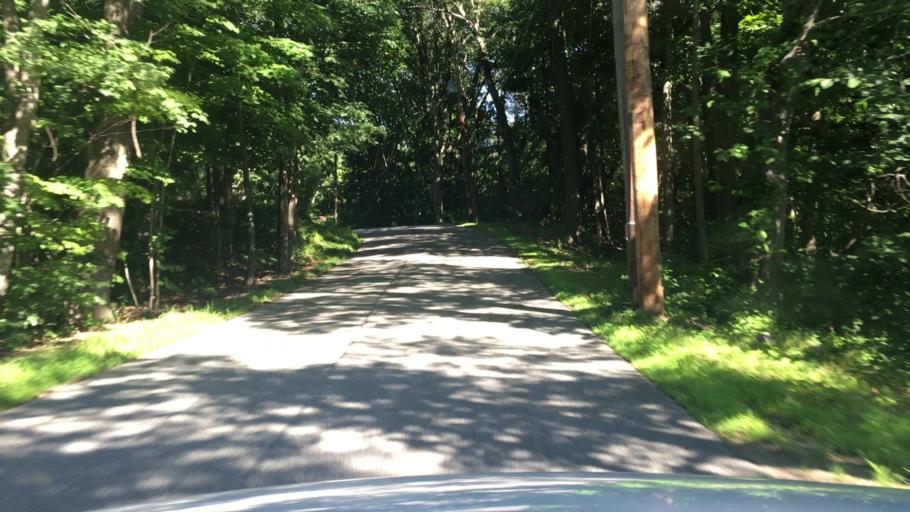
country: US
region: New Hampshire
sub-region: Rockingham County
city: Kensington
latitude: 42.9148
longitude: -70.9320
